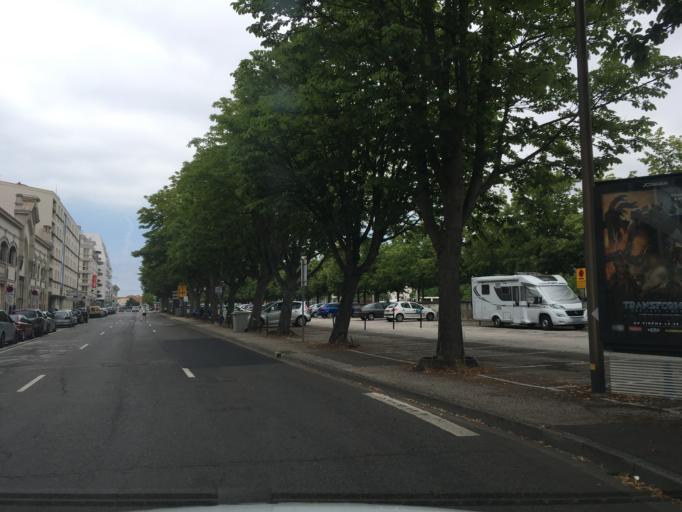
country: FR
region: Lorraine
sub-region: Departement de Meurthe-et-Moselle
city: Nancy
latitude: 48.6923
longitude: 6.1929
